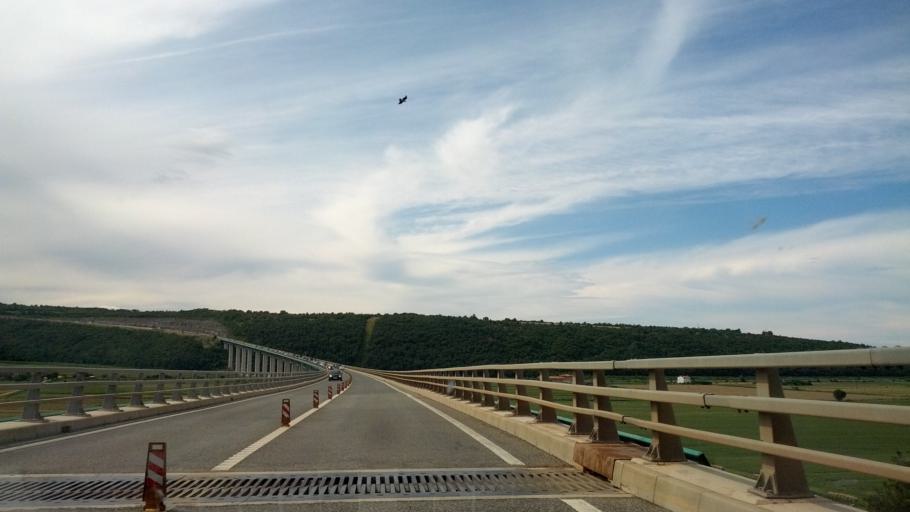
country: HR
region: Istarska
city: Novigrad
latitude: 45.3392
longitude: 13.6238
